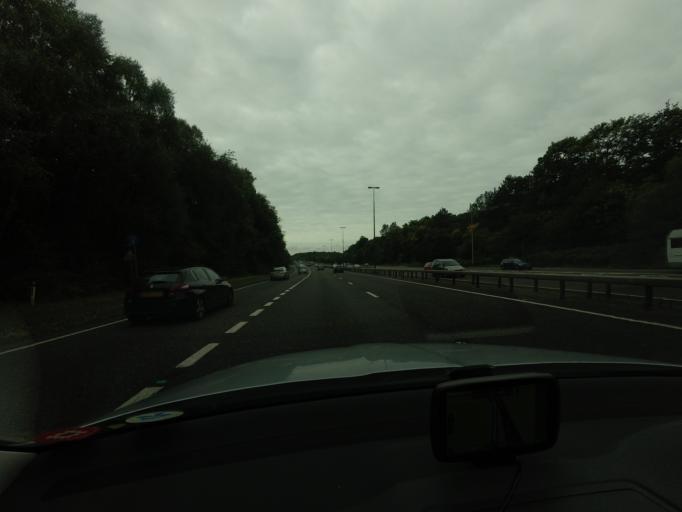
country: GB
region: England
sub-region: Surrey
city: Byfleet
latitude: 51.3263
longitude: -0.4461
